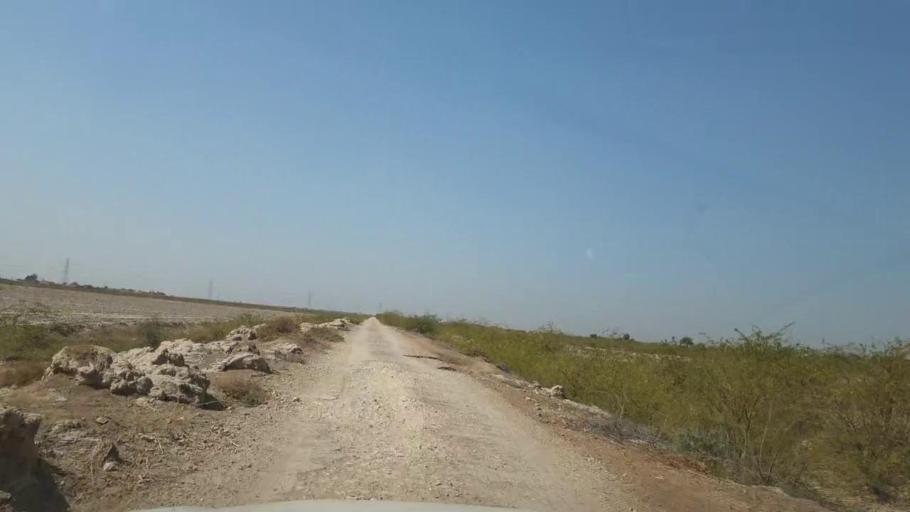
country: PK
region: Sindh
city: Kunri
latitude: 25.0964
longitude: 69.5026
